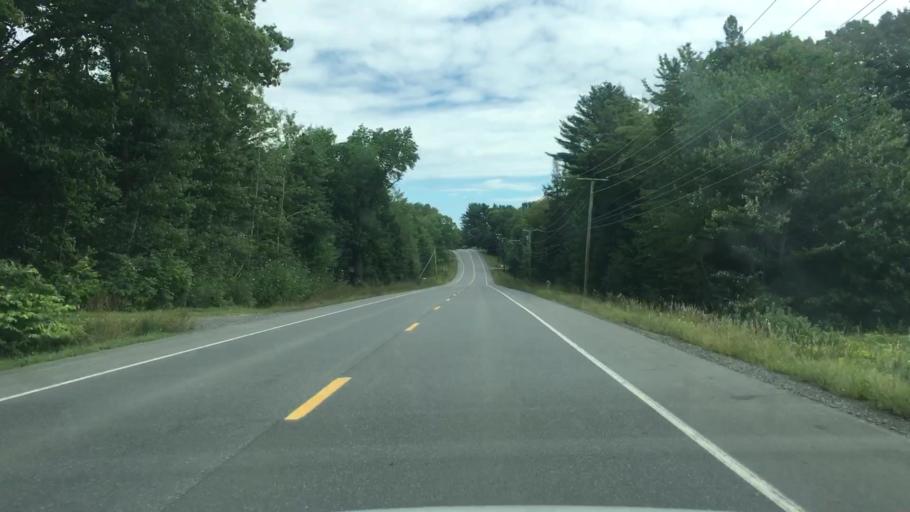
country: US
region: Maine
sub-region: Piscataquis County
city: Brownville
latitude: 45.2356
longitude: -69.0607
